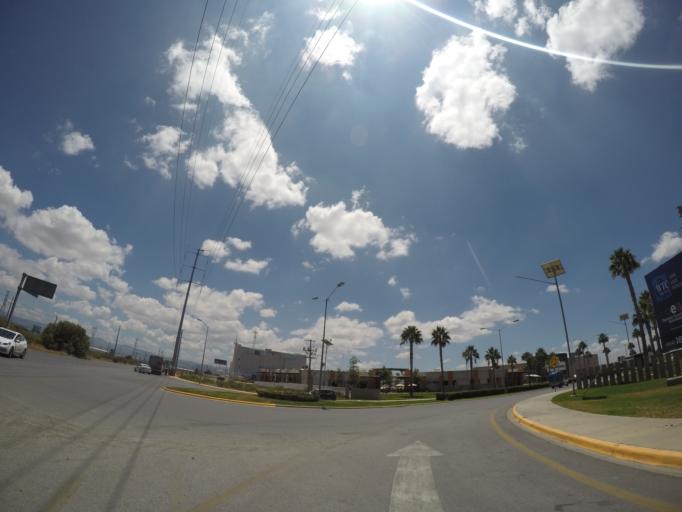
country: MX
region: San Luis Potosi
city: La Pila
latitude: 22.0421
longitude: -100.8940
